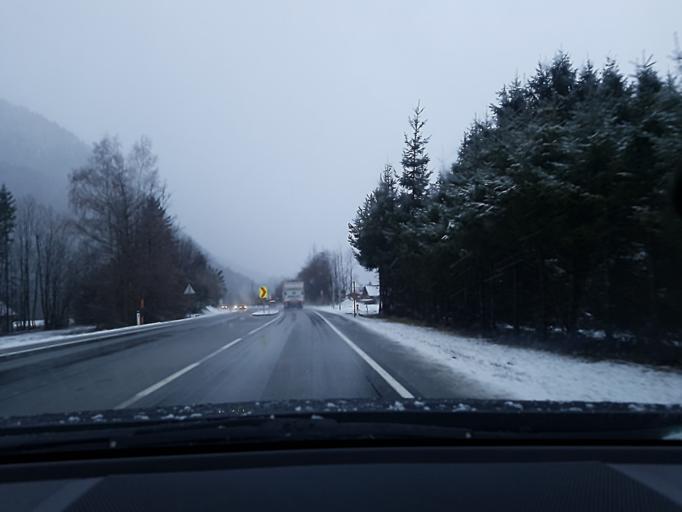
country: AT
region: Salzburg
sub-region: Politischer Bezirk Hallein
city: Scheffau am Tennengebirge
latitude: 47.5864
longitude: 13.2256
